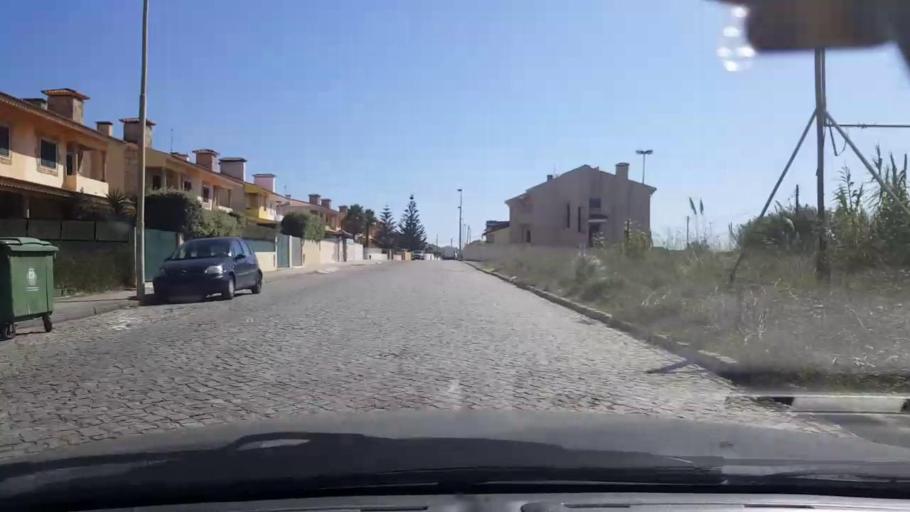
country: PT
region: Porto
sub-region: Vila do Conde
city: Arvore
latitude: 41.3028
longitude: -8.7358
